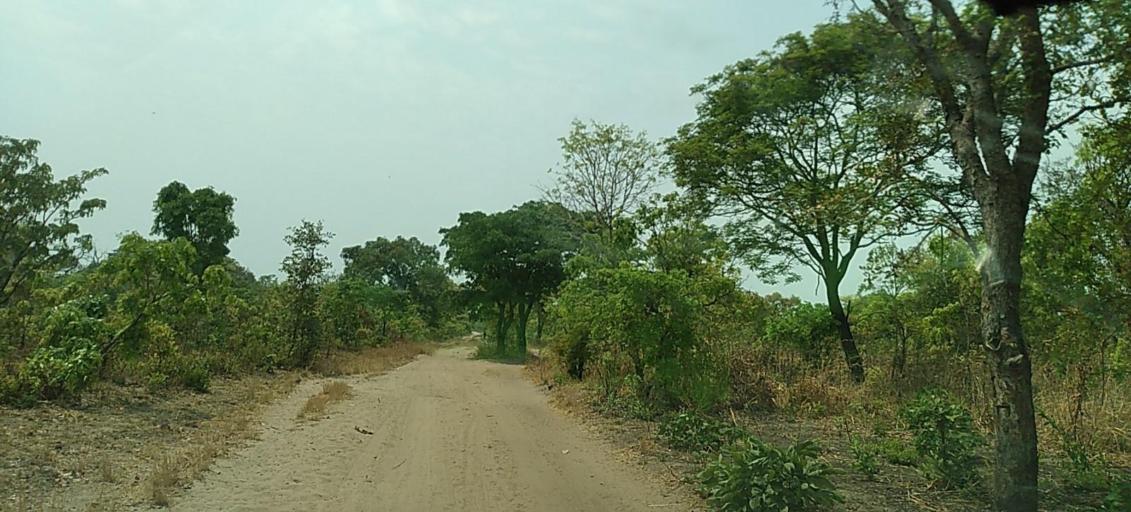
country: ZM
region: North-Western
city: Kabompo
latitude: -13.4632
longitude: 24.4291
